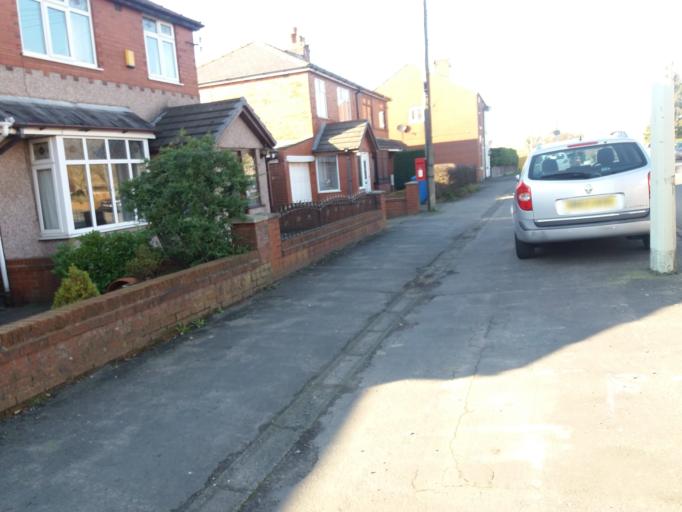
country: GB
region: England
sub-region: Lancashire
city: Adlington
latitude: 53.6235
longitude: -2.6064
